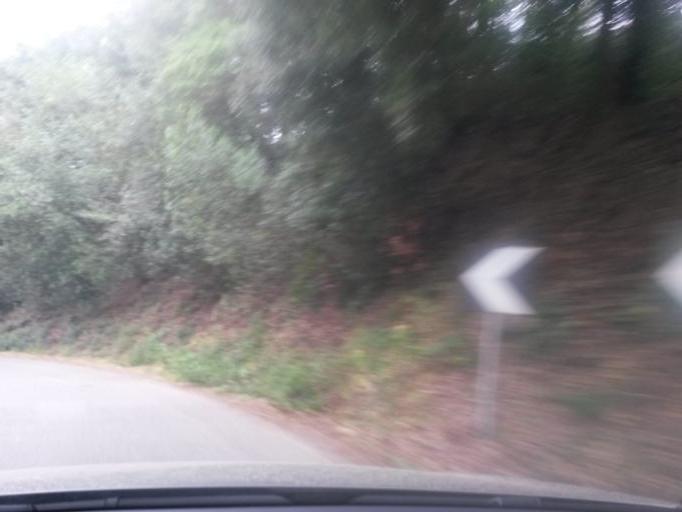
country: IT
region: Tuscany
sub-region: Provincia di Livorno
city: Capoliveri
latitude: 42.7487
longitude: 10.3756
